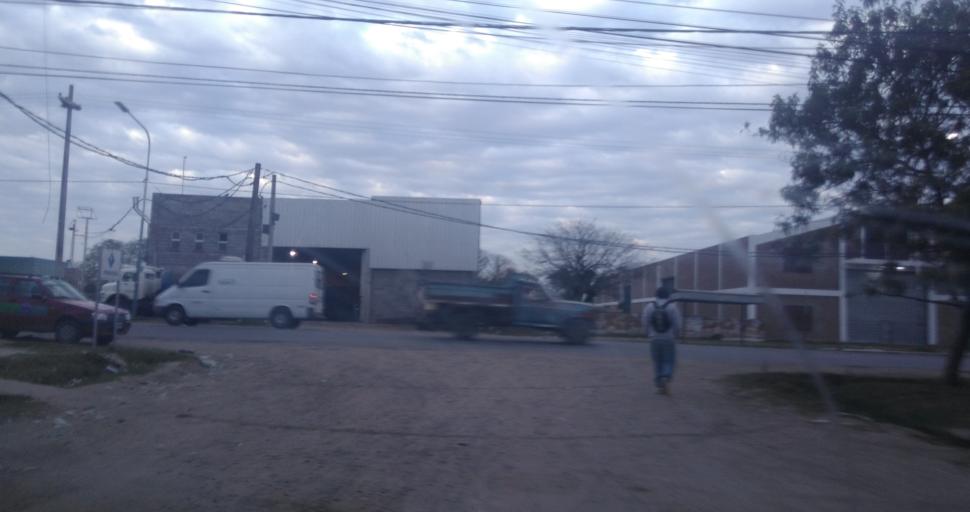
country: AR
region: Chaco
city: Fontana
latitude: -27.4261
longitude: -59.0287
